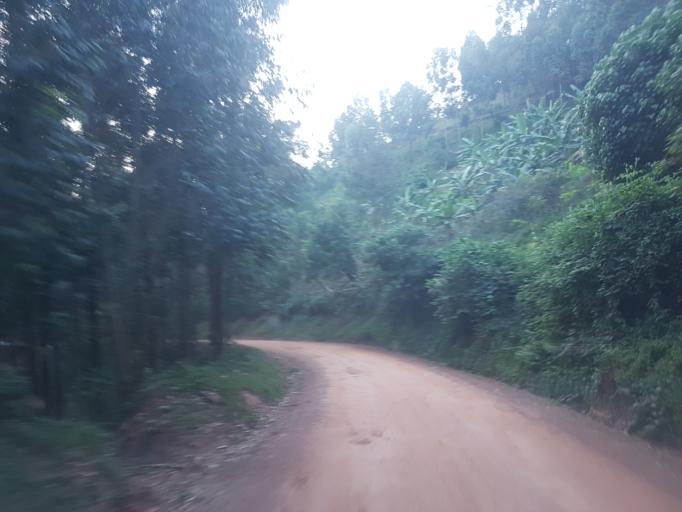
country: UG
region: Western Region
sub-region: Kanungu District
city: Kanungu
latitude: -0.9507
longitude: 29.8283
